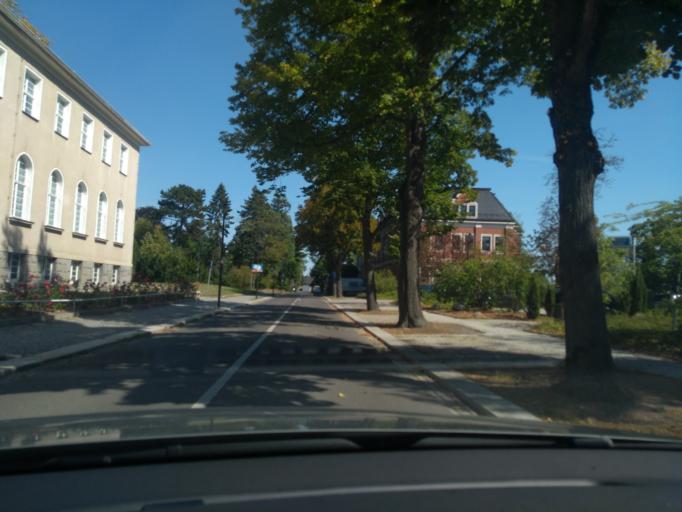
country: DE
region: Saxony
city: Kamenz
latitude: 51.2719
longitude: 14.0951
